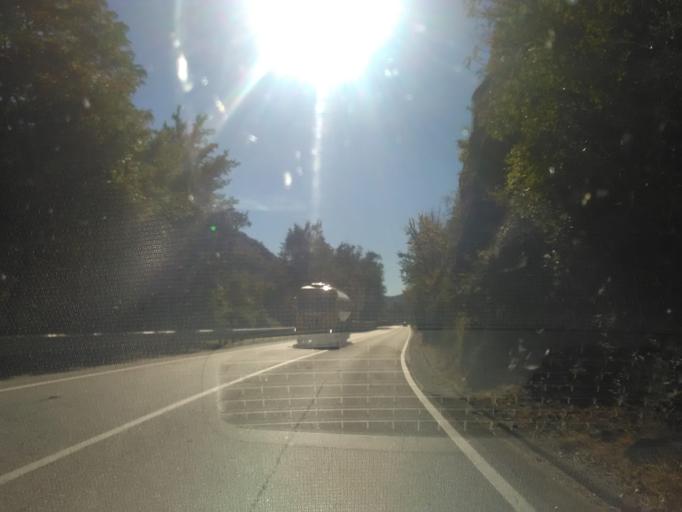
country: IT
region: Piedmont
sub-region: Provincia di Vercelli
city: Quarona
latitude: 45.7496
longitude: 8.2599
